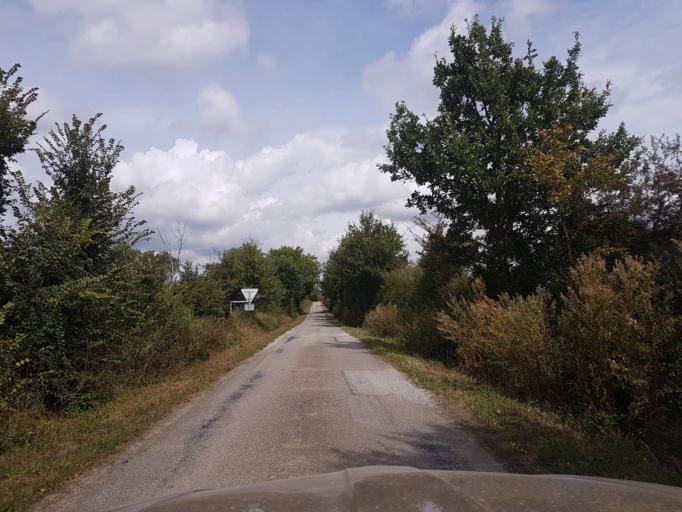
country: FR
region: Pays de la Loire
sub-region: Departement de la Loire-Atlantique
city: Petit-Mars
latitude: 47.4128
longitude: -1.4470
